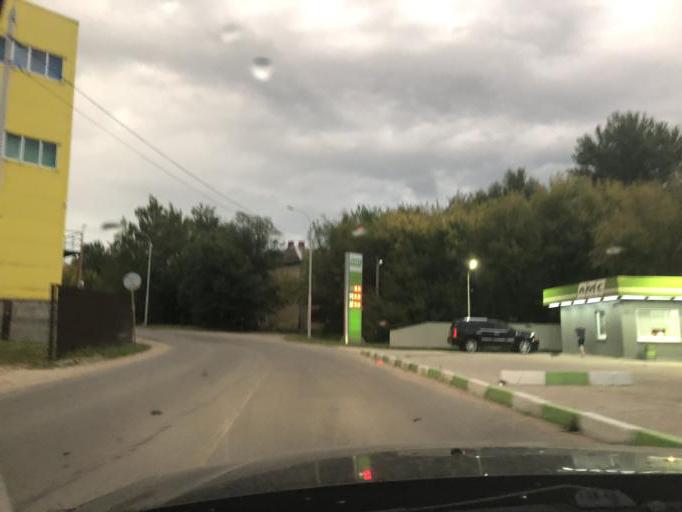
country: RU
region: Tula
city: Tula
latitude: 54.2258
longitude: 37.6137
